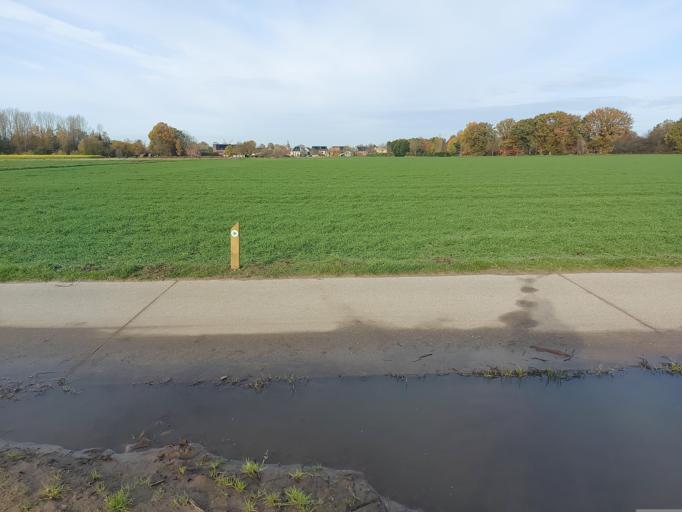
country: BE
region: Flanders
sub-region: Provincie Antwerpen
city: Geel
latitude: 51.1596
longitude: 4.9515
